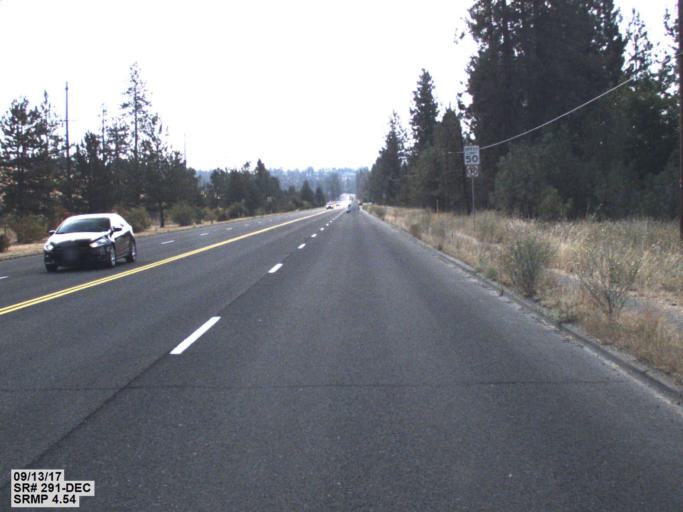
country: US
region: Washington
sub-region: Spokane County
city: Town and Country
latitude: 47.7292
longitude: -117.4999
